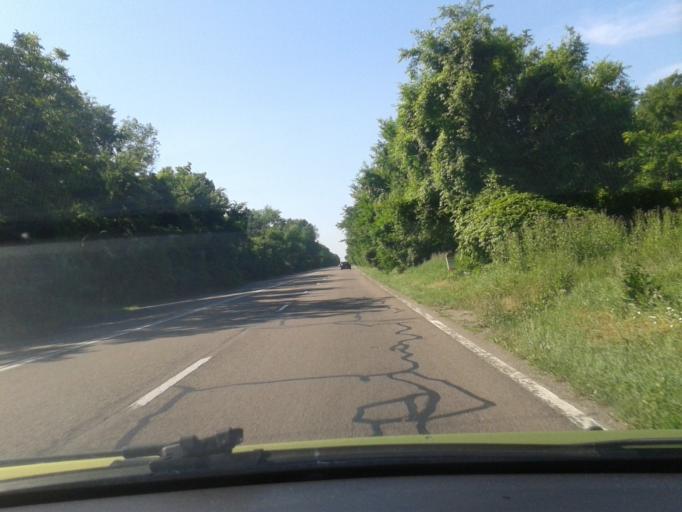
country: RO
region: Constanta
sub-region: Comuna Douazeci si Trei August
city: Dulcesti
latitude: 43.8677
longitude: 28.5748
